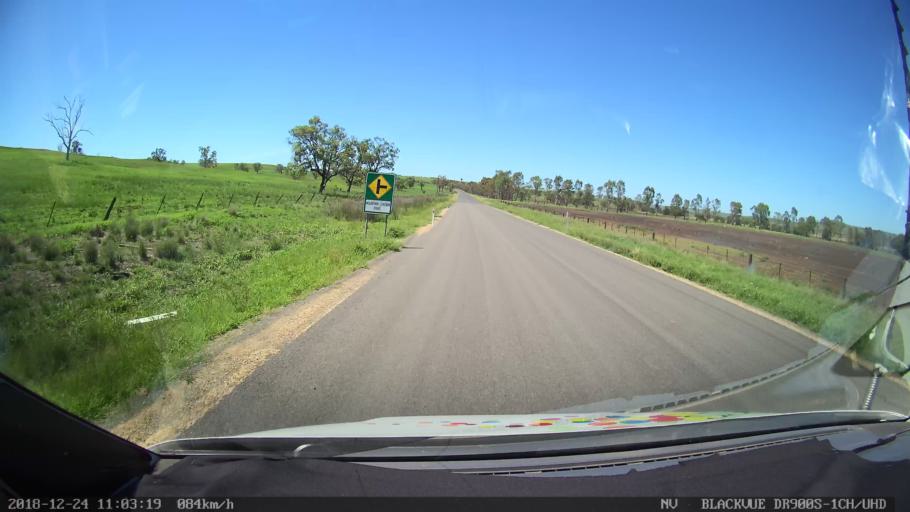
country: AU
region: New South Wales
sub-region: Upper Hunter Shire
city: Merriwa
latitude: -32.0950
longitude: 150.3688
